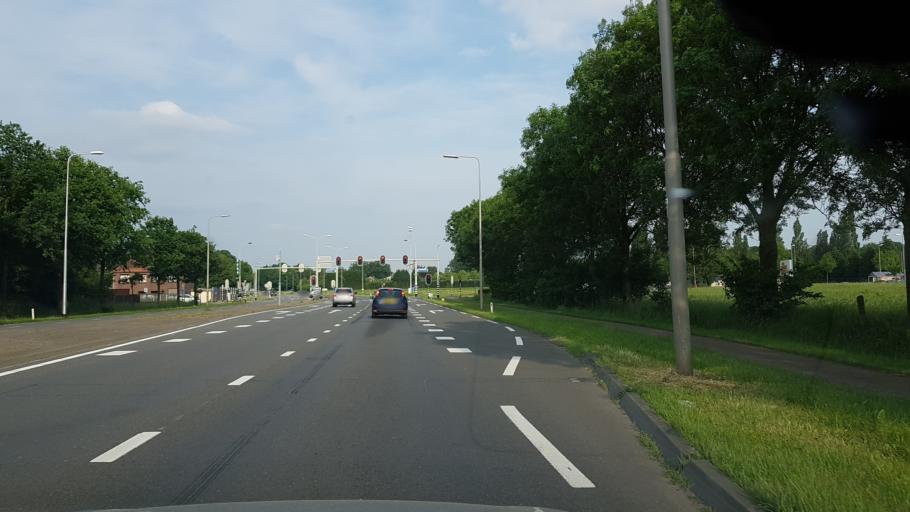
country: NL
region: Limburg
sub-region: Gemeente Sittard-Geleen
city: Limbricht
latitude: 50.9921
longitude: 5.8235
